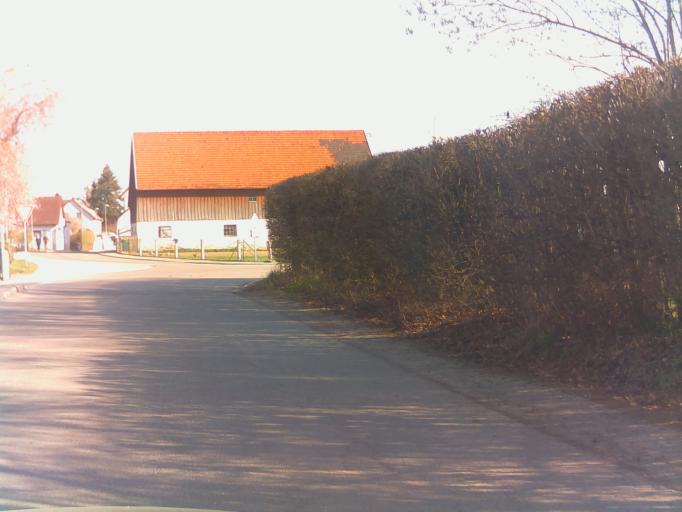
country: DE
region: Bavaria
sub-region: Swabia
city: Pottmes
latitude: 48.5869
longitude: 11.0830
